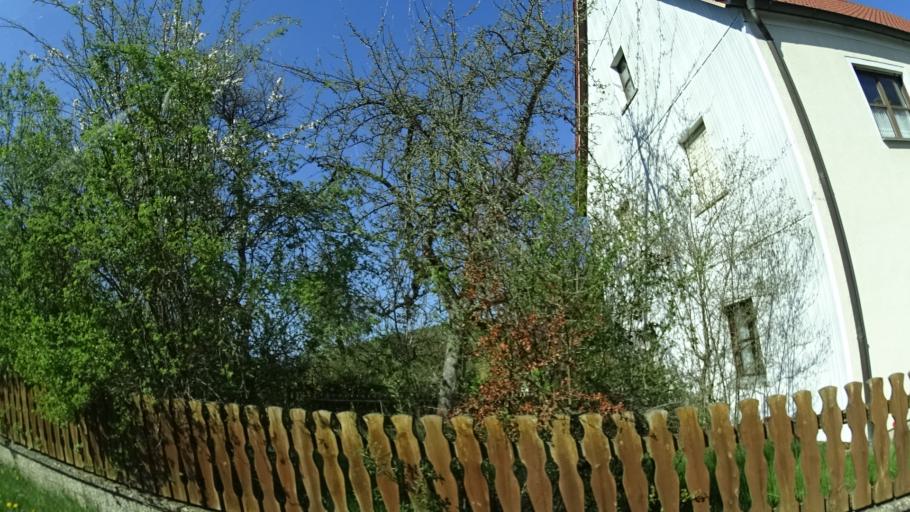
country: DE
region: Bavaria
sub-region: Upper Palatinate
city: Edelsfeld
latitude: 49.5472
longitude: 11.7265
